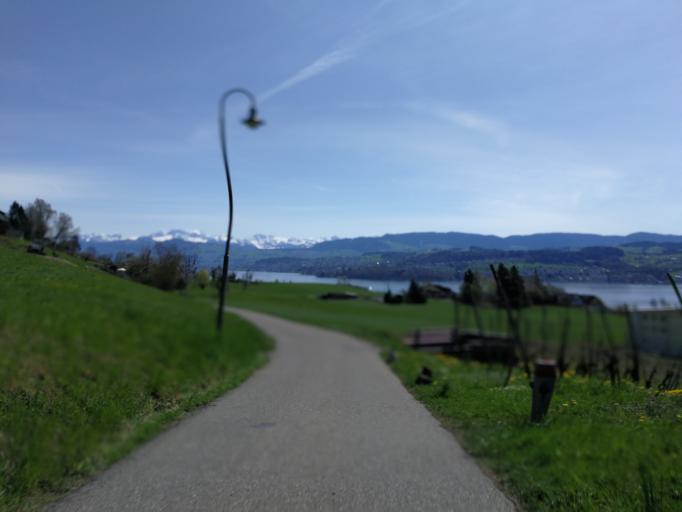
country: CH
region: Zurich
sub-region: Bezirk Meilen
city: Feldmeilen
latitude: 47.2761
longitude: 8.6299
